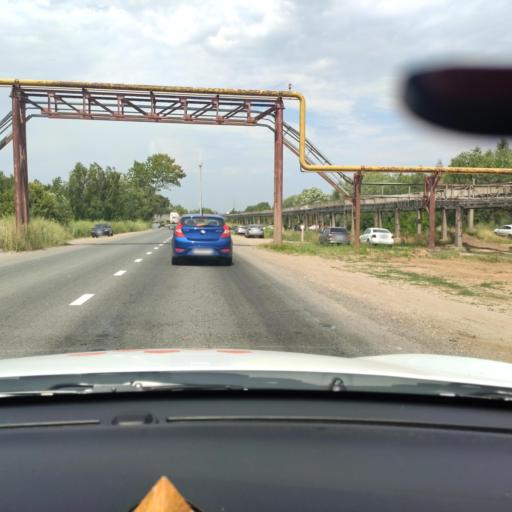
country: RU
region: Tatarstan
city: Staroye Arakchino
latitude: 55.8801
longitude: 48.9761
